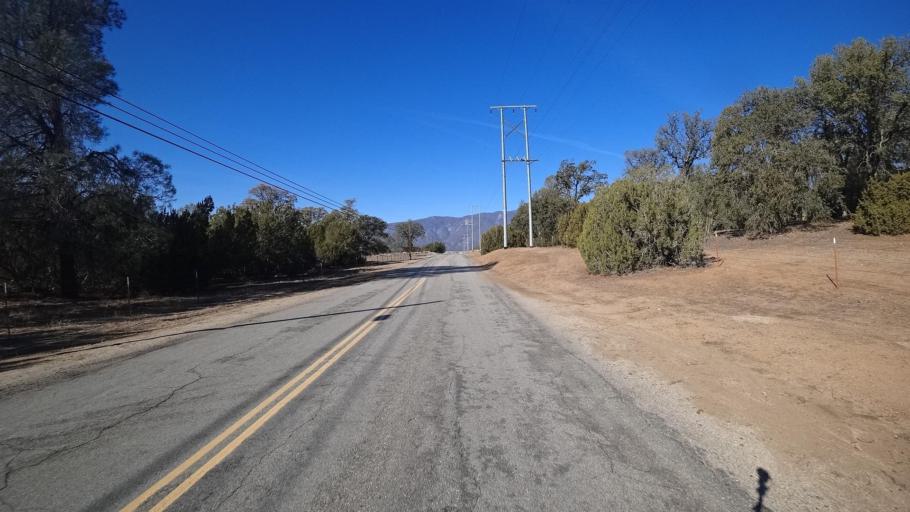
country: US
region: California
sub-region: Kern County
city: Bodfish
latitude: 35.4026
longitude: -118.4794
